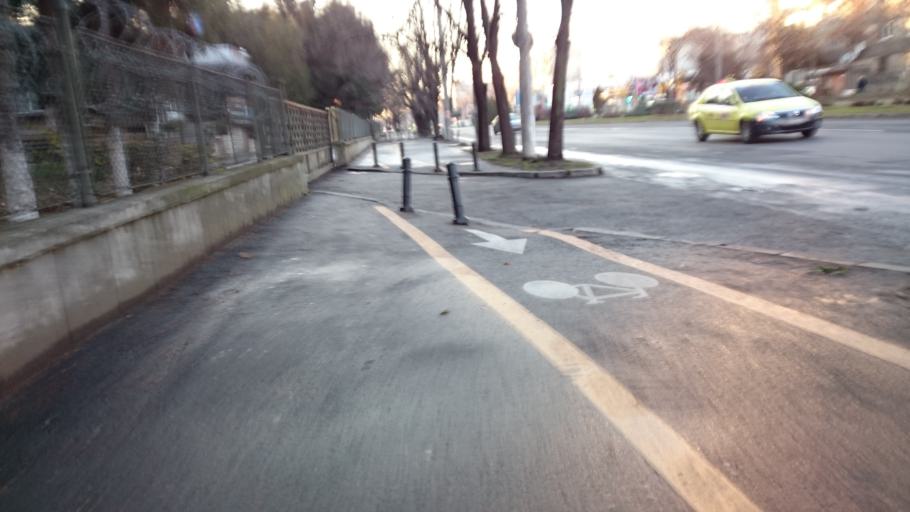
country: RO
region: Bucuresti
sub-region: Municipiul Bucuresti
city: Bucuresti
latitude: 44.4255
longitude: 26.0539
